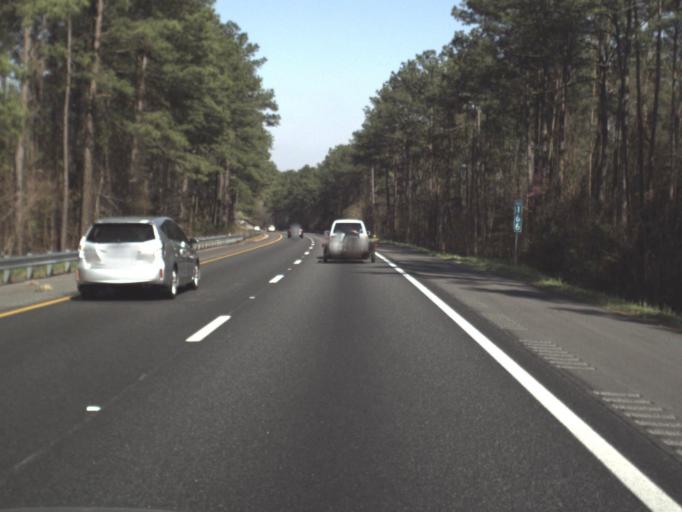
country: US
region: Florida
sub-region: Gadsden County
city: Chattahoochee
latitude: 30.6185
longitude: -84.8132
